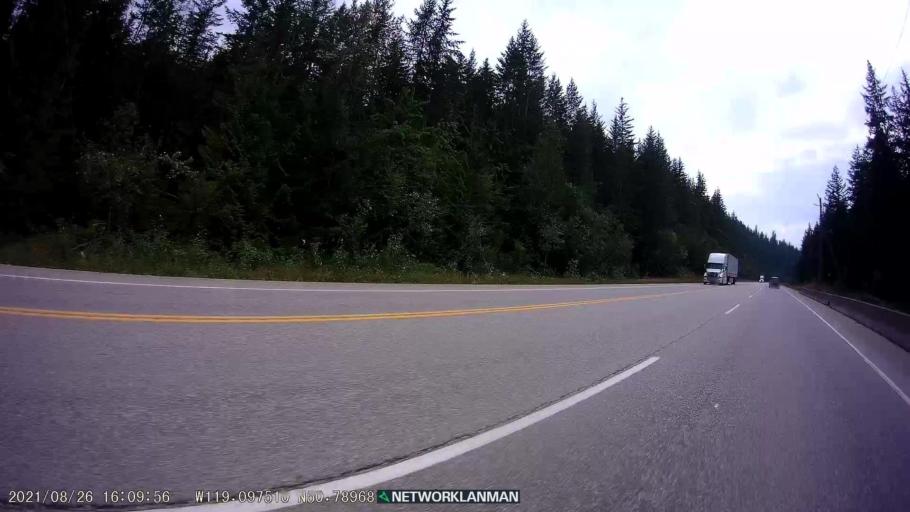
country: CA
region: British Columbia
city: Sicamous
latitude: 50.7897
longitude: -119.0979
